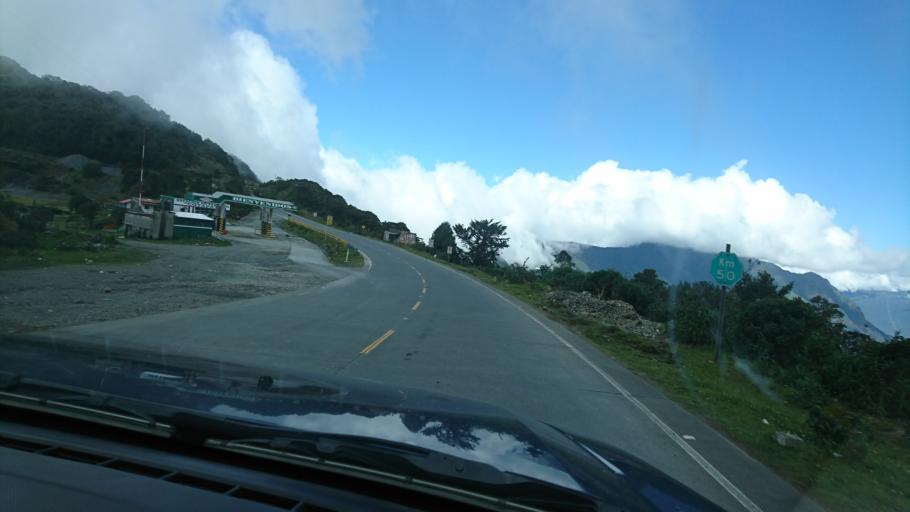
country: BO
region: La Paz
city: Coroico
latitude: -16.2869
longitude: -67.8505
